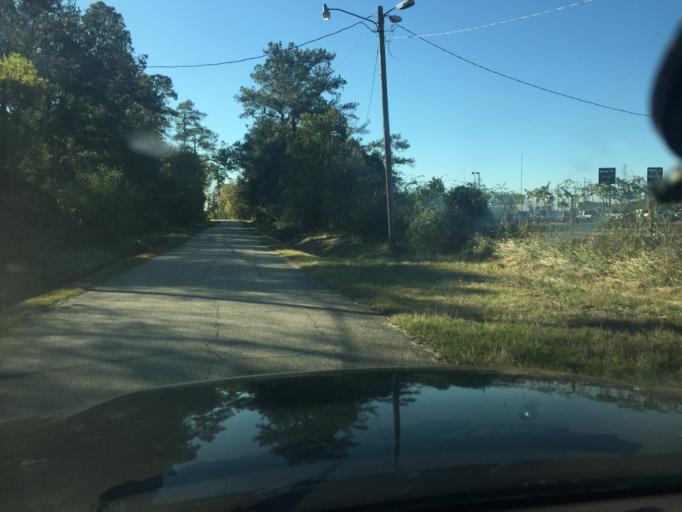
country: US
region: Louisiana
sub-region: Saint Tammany Parish
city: Slidell
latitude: 30.2442
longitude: -89.7635
